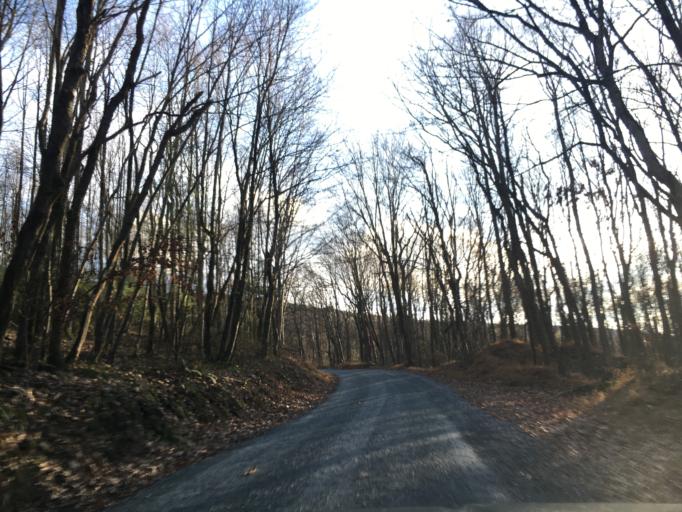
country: US
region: Pennsylvania
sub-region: Carbon County
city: Lehighton
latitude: 40.7698
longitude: -75.7104
